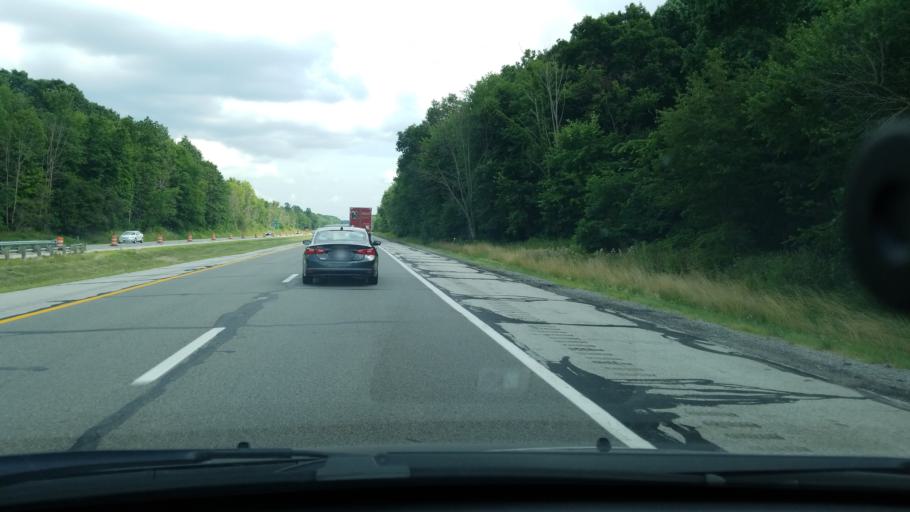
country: US
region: Ohio
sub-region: Mahoning County
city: Austintown
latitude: 41.0634
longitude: -80.7843
